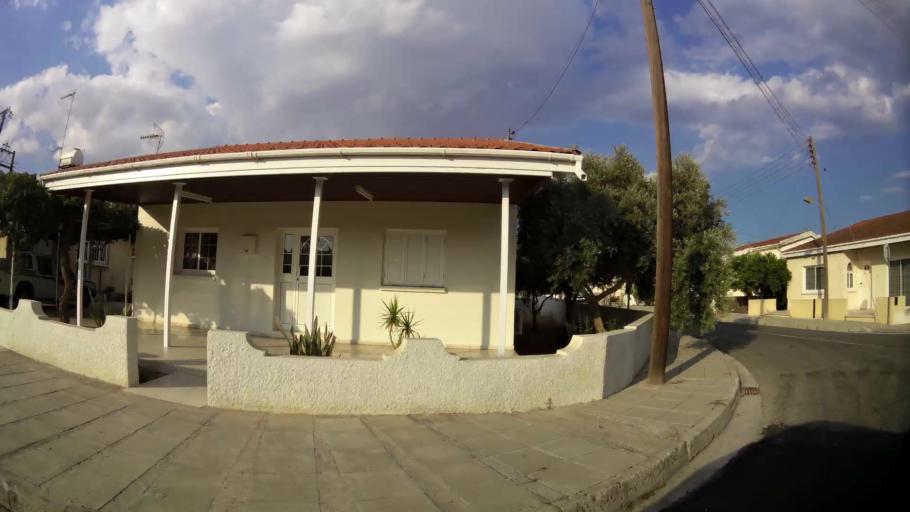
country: CY
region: Larnaka
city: Dhromolaxia
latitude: 34.8725
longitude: 33.5866
